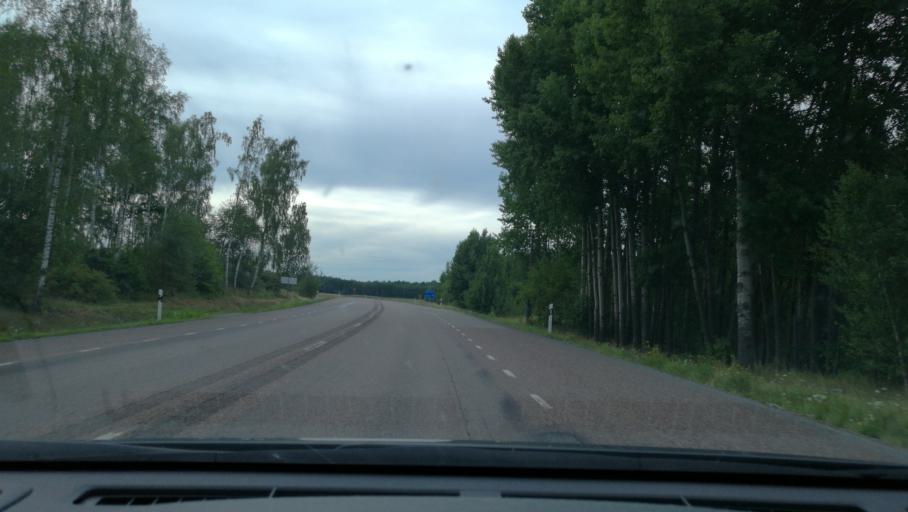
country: SE
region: Vaestmanland
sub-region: Kopings Kommun
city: Koping
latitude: 59.4804
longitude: 15.9874
